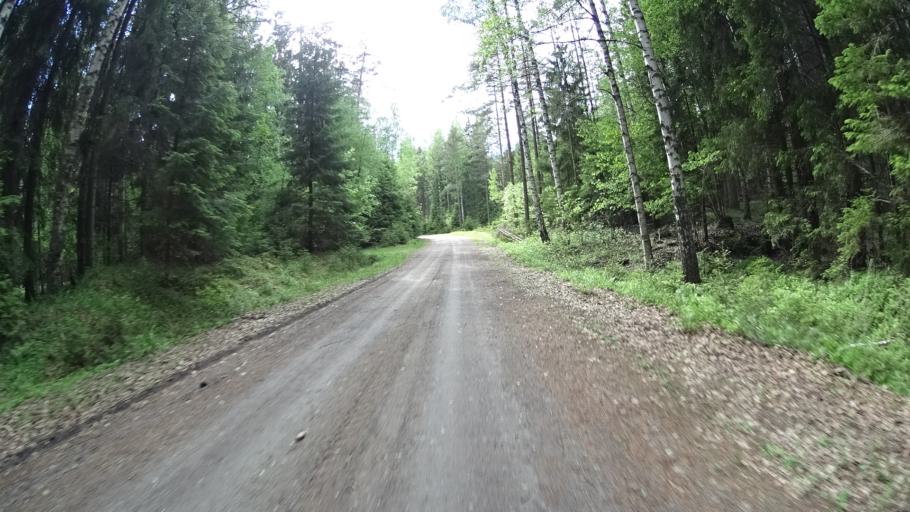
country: FI
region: Varsinais-Suomi
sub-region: Salo
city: Kisko
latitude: 60.1809
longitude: 23.5347
